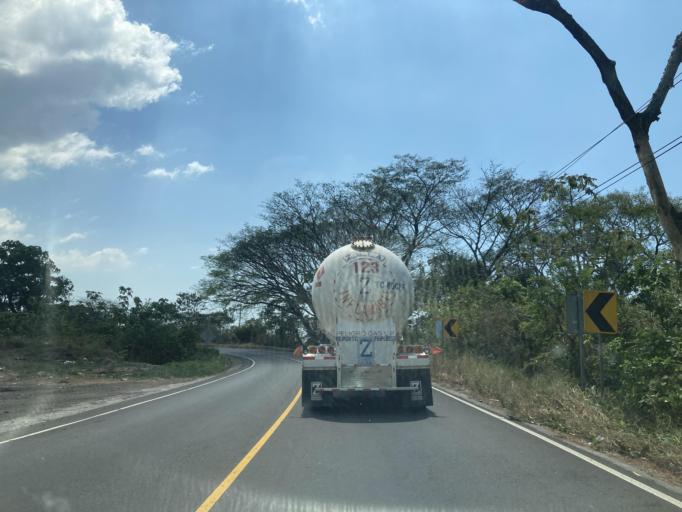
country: GT
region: Santa Rosa
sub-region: Municipio de Taxisco
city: Taxisco
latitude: 14.0985
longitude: -90.5320
